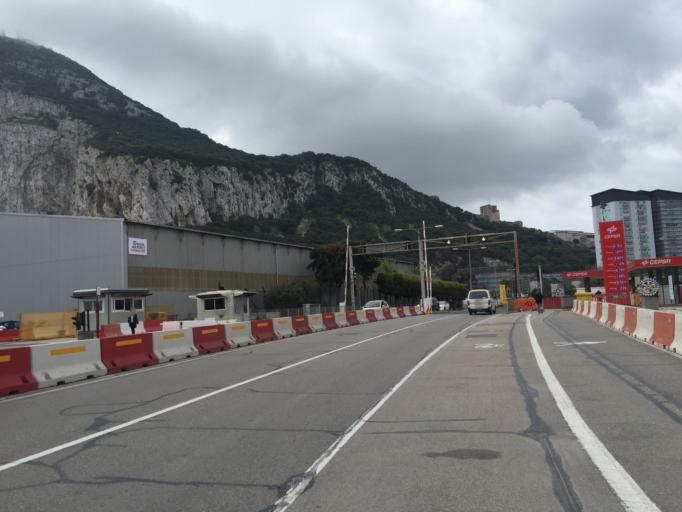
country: GI
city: Gibraltar
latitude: 36.1505
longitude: -5.3489
